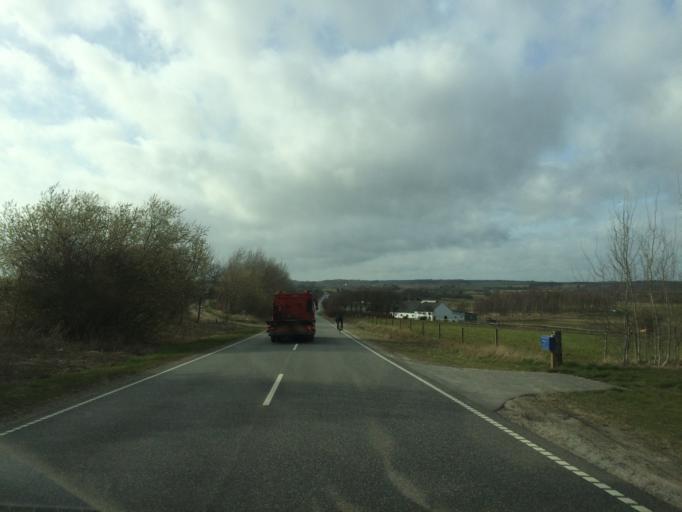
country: DK
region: Central Jutland
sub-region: Randers Kommune
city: Langa
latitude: 56.4850
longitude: 9.8695
